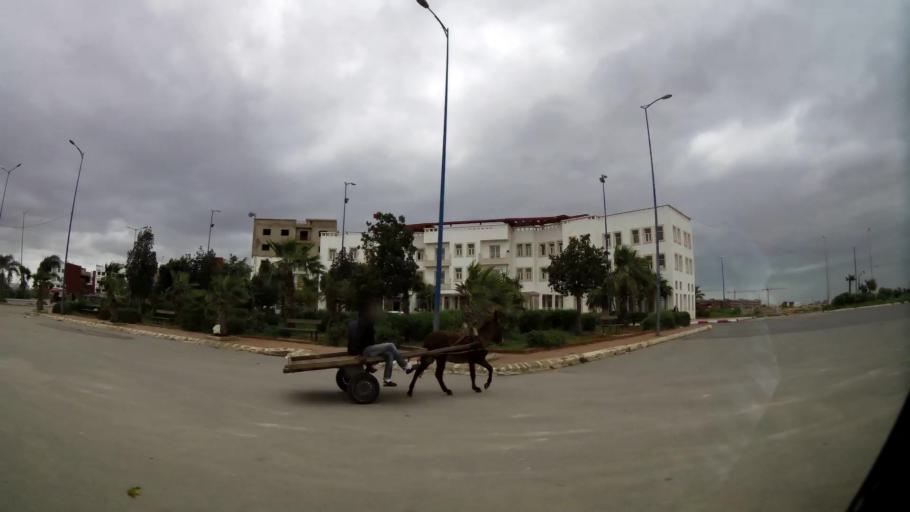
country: MA
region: Grand Casablanca
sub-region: Mediouna
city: Tit Mellil
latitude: 33.5515
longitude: -7.5311
